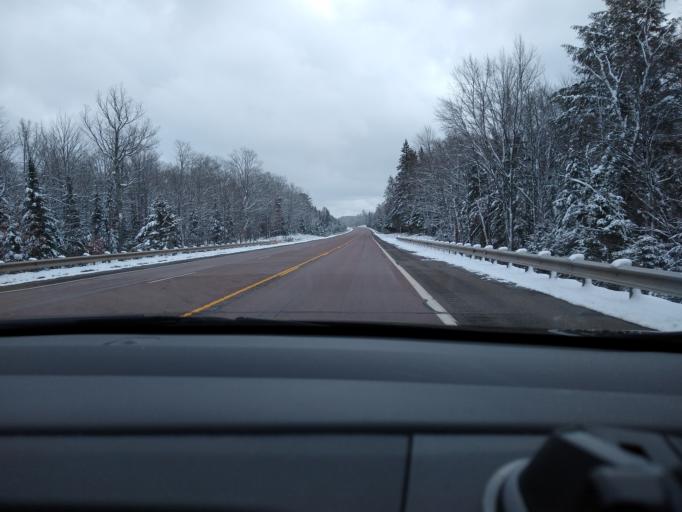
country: US
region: Wisconsin
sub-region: Vilas County
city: Eagle River
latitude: 46.1996
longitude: -89.0110
